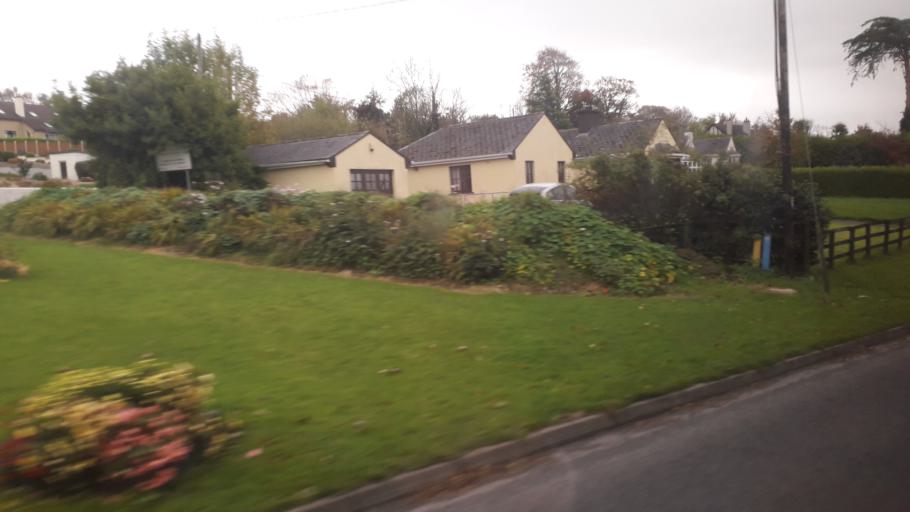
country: IE
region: Munster
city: Ballina
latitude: 52.7994
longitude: -8.4340
